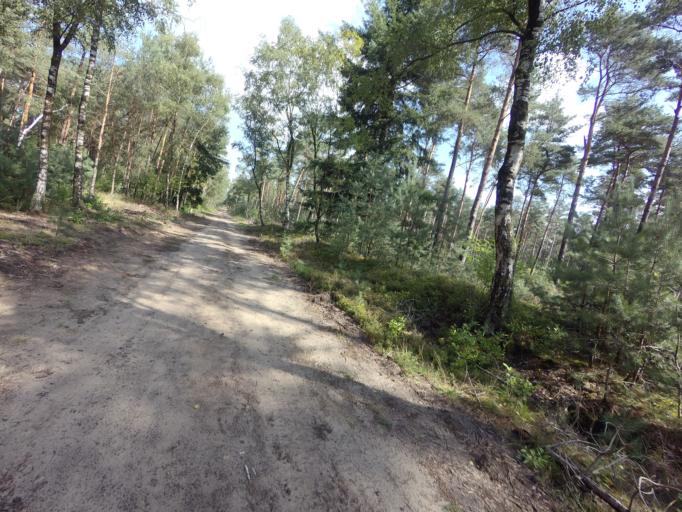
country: NL
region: Gelderland
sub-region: Gemeente Renkum
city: Wolfheze
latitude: 52.0396
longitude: 5.7637
